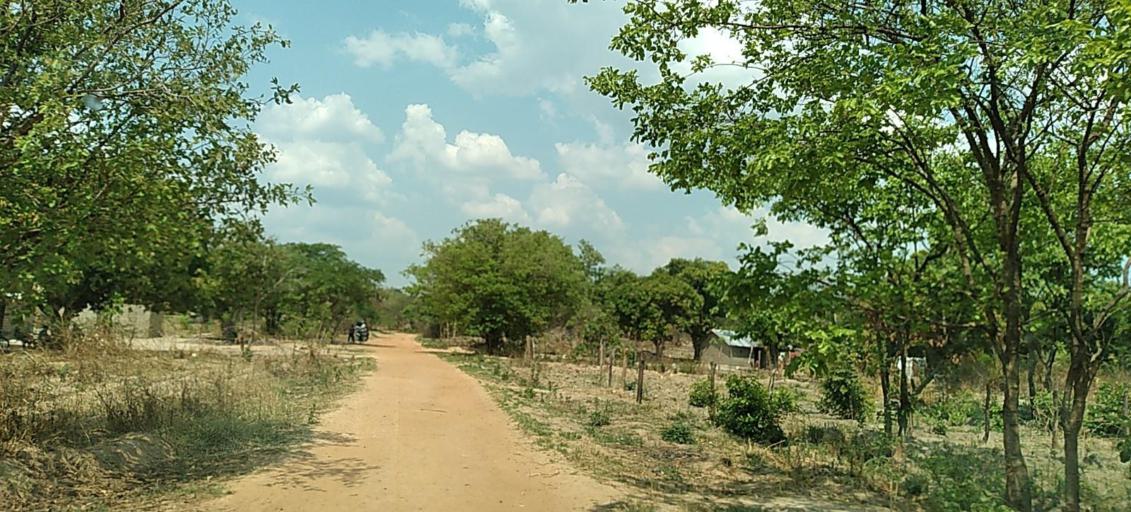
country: ZM
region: Copperbelt
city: Luanshya
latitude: -13.1547
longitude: 28.3158
